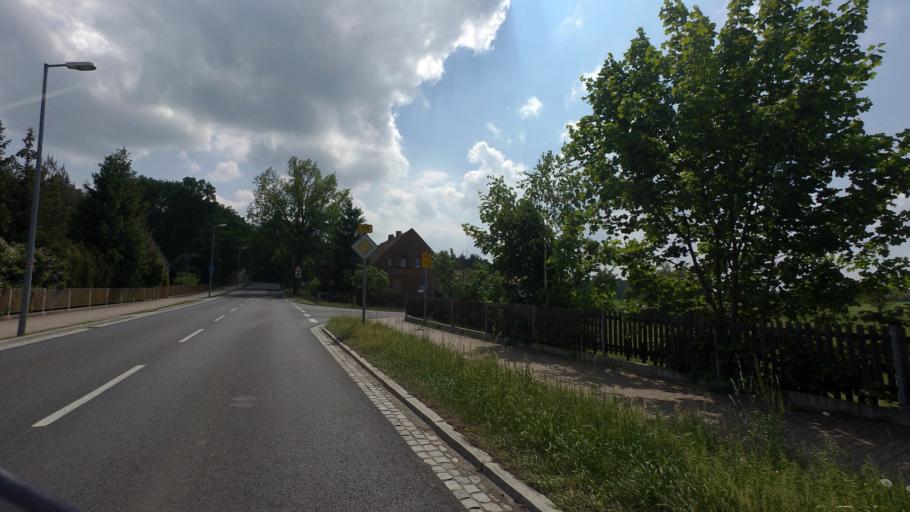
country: DE
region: Saxony
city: Rietschen
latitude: 51.3905
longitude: 14.7851
